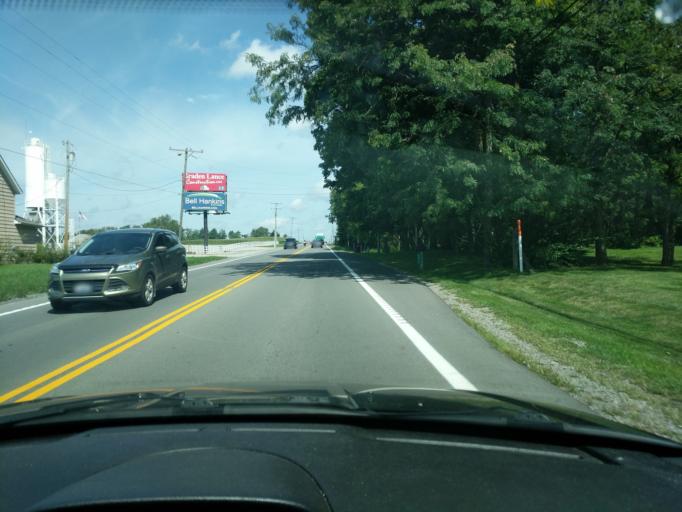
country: US
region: Ohio
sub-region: Logan County
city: West Liberty
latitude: 40.3036
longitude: -83.7594
